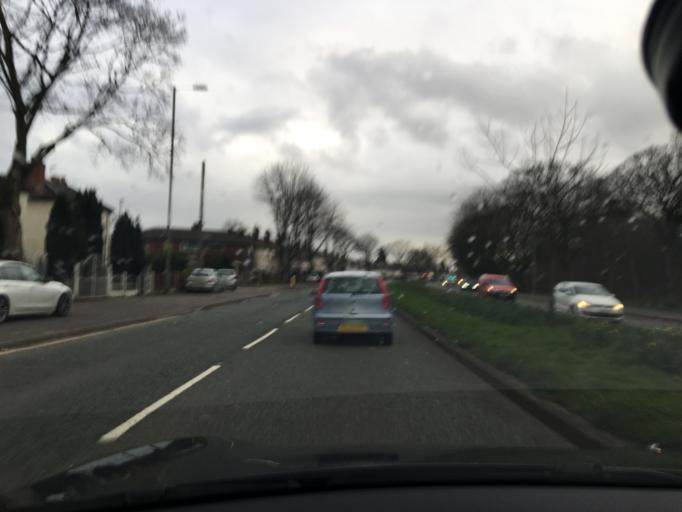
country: GB
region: England
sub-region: Manchester
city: Chorlton cum Hardy
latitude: 53.4390
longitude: -2.2440
